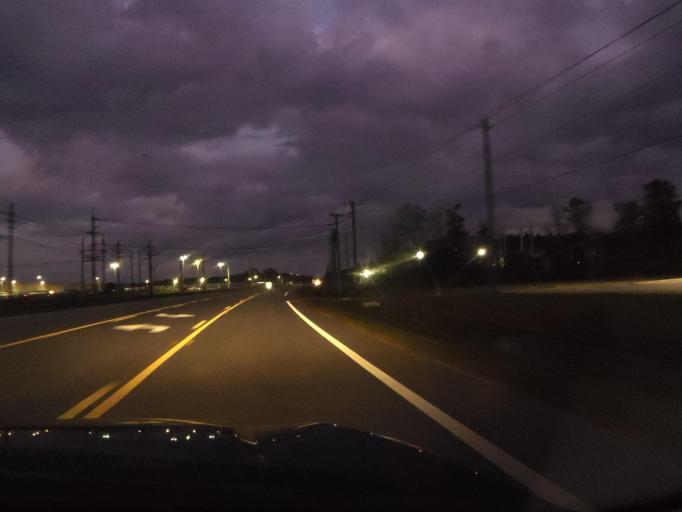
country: US
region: Florida
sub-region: Putnam County
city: Palatka
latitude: 29.6765
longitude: -81.6782
